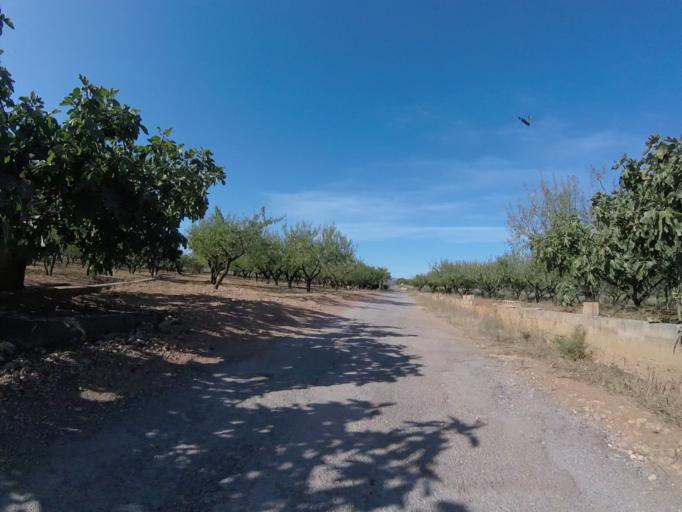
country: ES
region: Valencia
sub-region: Provincia de Castello
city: Torreblanca
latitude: 40.2102
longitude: 0.2294
